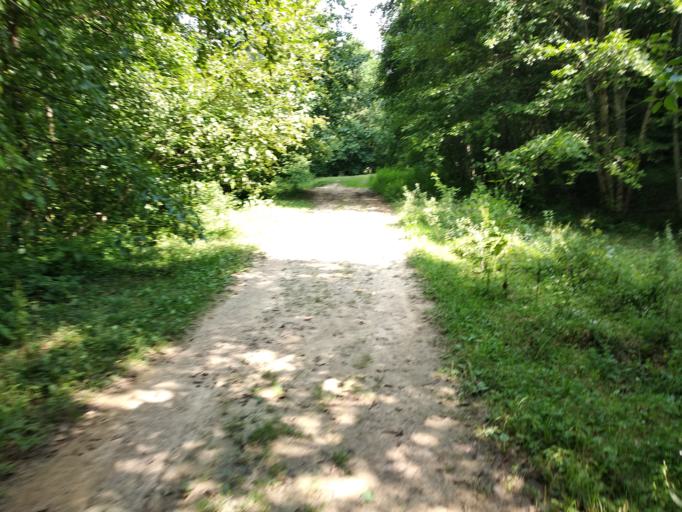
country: RU
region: Adygeya
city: Kamennomostskiy
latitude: 44.1948
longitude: 39.9518
